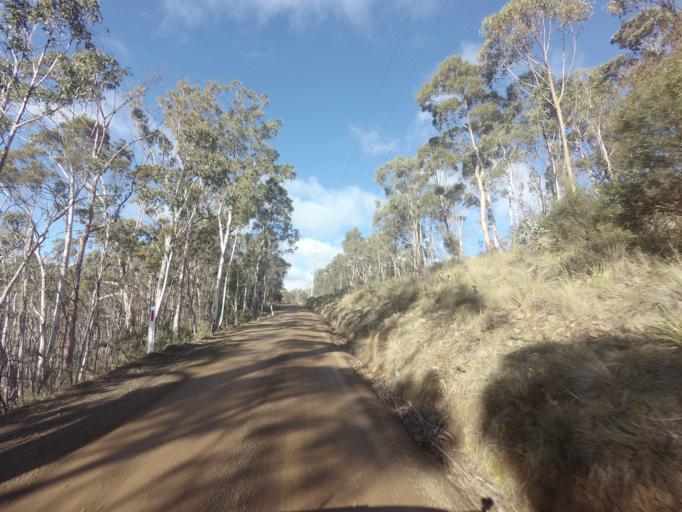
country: AU
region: Tasmania
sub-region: Derwent Valley
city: New Norfolk
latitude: -42.8328
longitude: 147.1254
